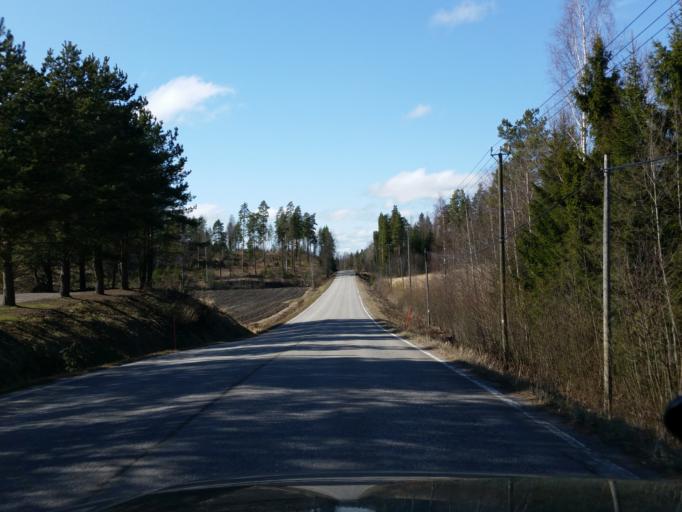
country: FI
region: Uusimaa
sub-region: Helsinki
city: Vihti
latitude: 60.4223
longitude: 24.2698
